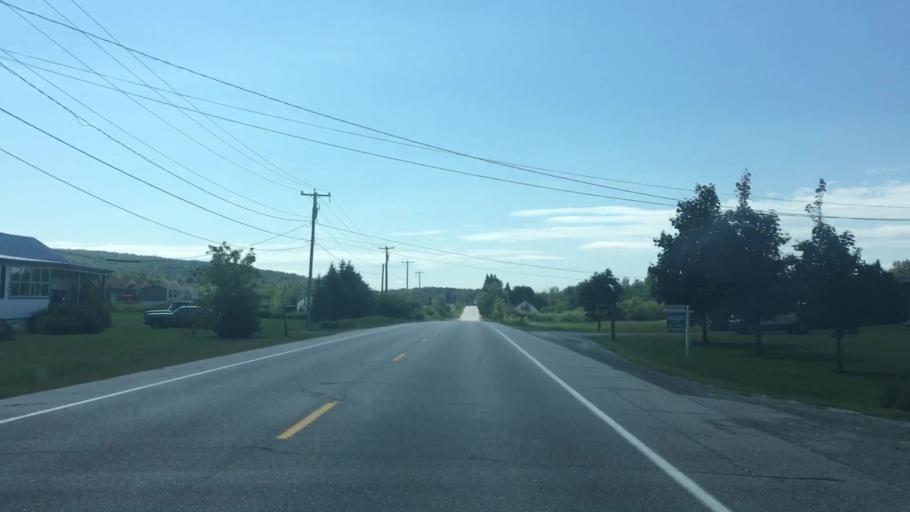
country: US
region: Maine
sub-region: Kennebec County
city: Monmouth
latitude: 44.1773
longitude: -69.9987
